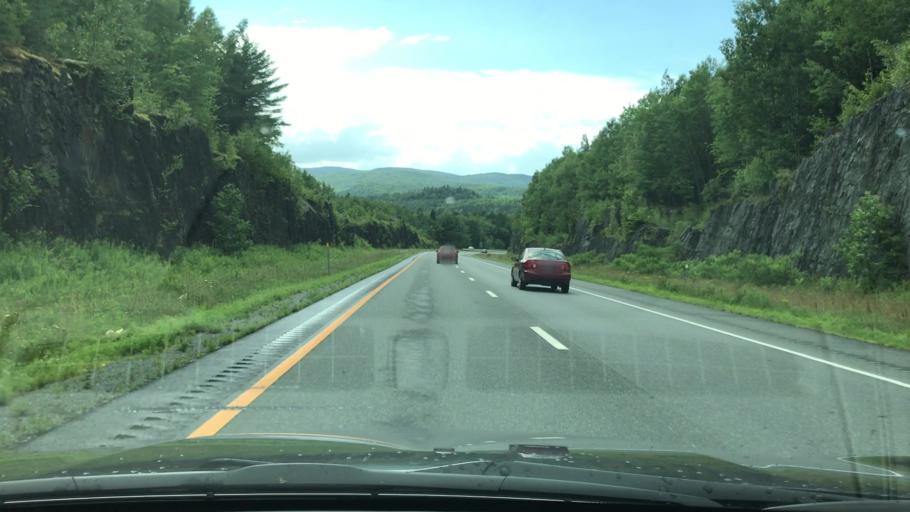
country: US
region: New Hampshire
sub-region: Grafton County
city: Littleton
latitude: 44.3136
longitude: -71.8472
